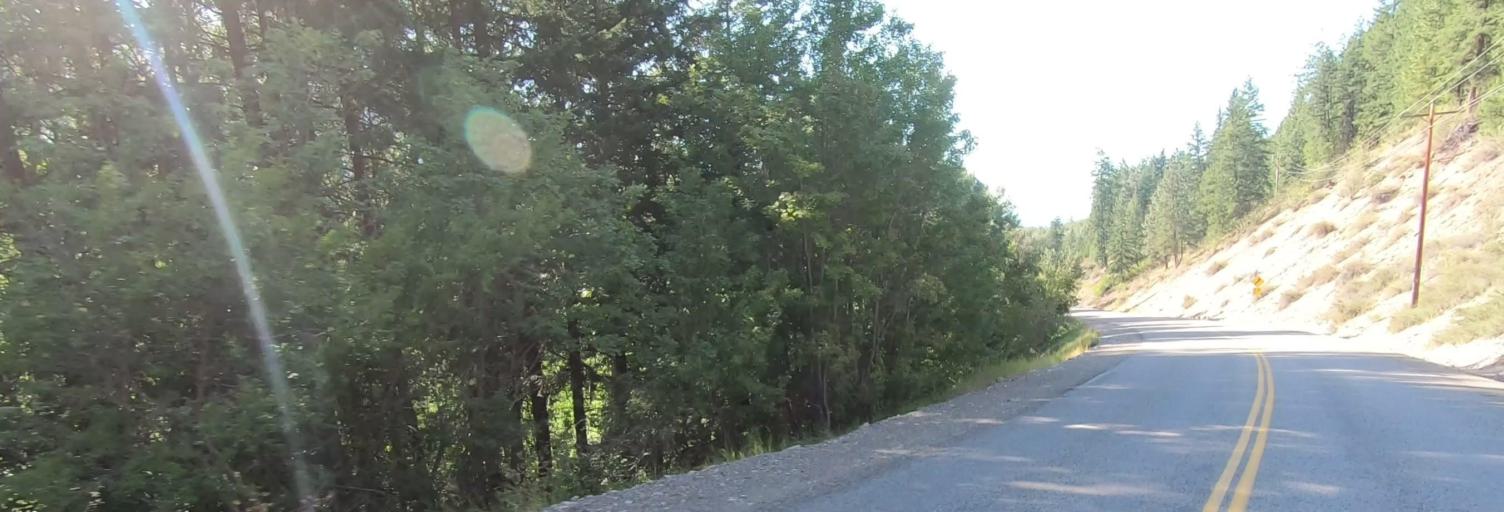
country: US
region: Washington
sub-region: Chelan County
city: Granite Falls
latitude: 48.5488
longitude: -120.3278
